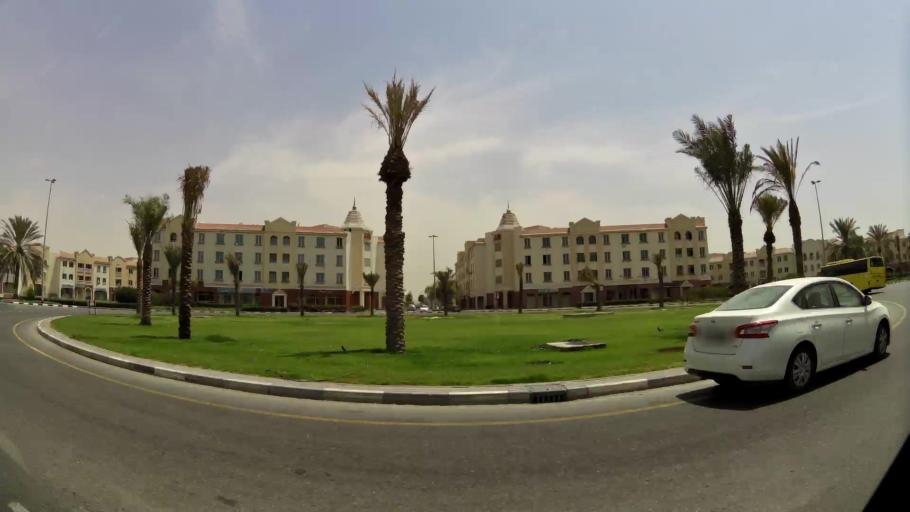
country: AE
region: Ash Shariqah
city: Sharjah
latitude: 25.1753
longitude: 55.4054
